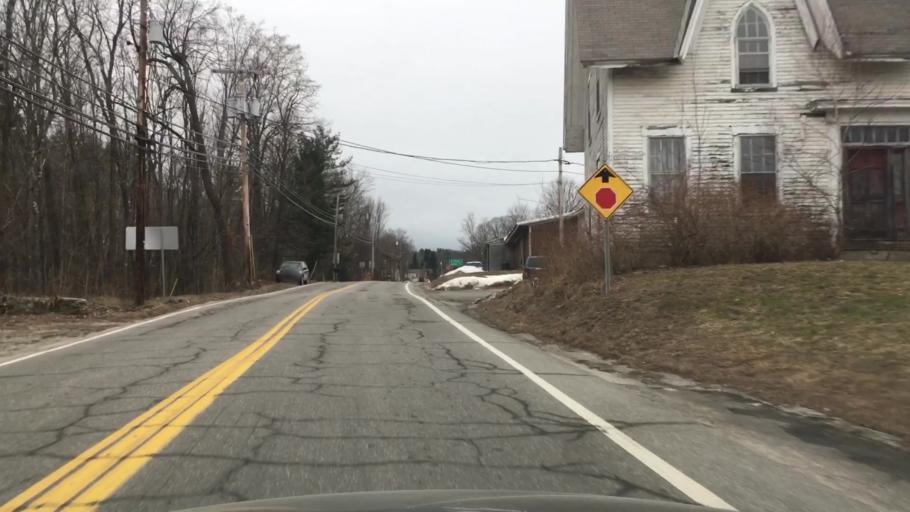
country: US
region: New Hampshire
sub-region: Hillsborough County
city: Weare
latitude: 43.0550
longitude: -71.7141
